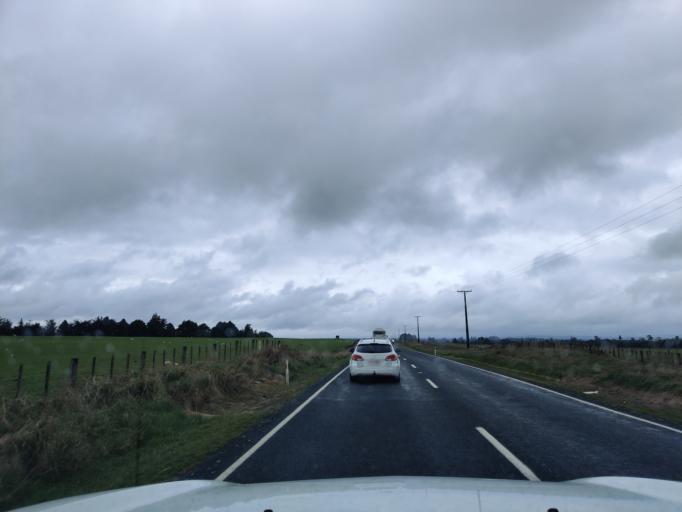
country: NZ
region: Manawatu-Wanganui
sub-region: Ruapehu District
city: Waiouru
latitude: -39.3581
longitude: 175.3506
